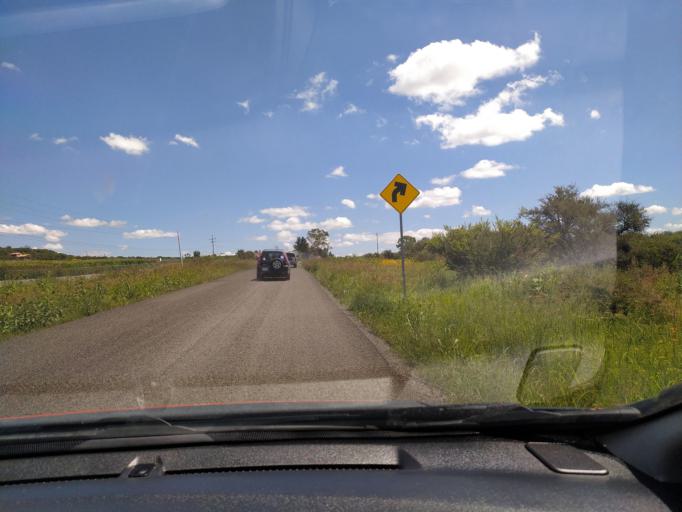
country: MX
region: Jalisco
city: San Diego de Alejandria
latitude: 21.0038
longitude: -102.0847
